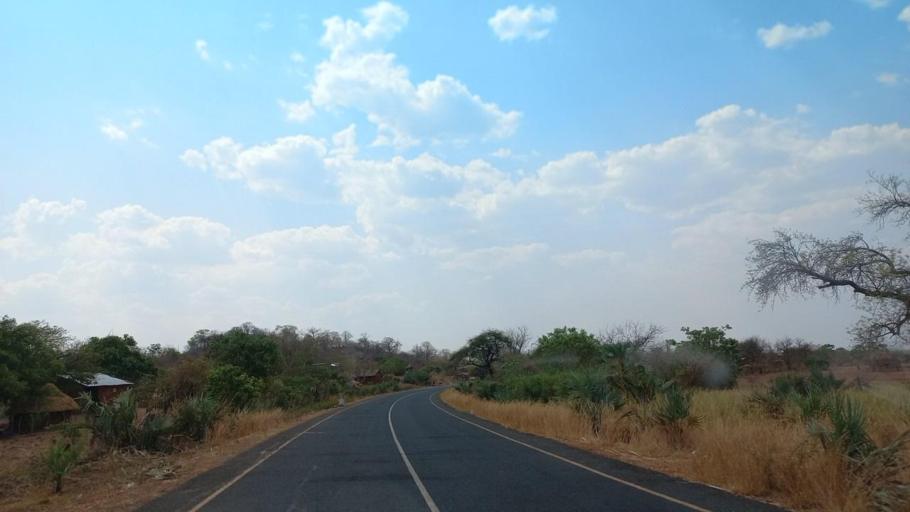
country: ZM
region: Lusaka
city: Luangwa
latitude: -15.3173
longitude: 30.3319
